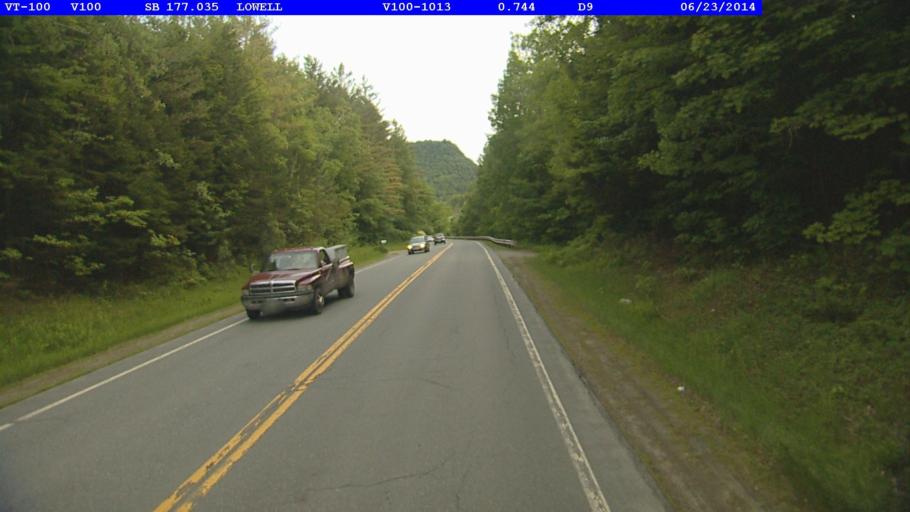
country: US
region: Vermont
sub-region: Lamoille County
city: Hyde Park
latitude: 44.7496
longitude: -72.4604
